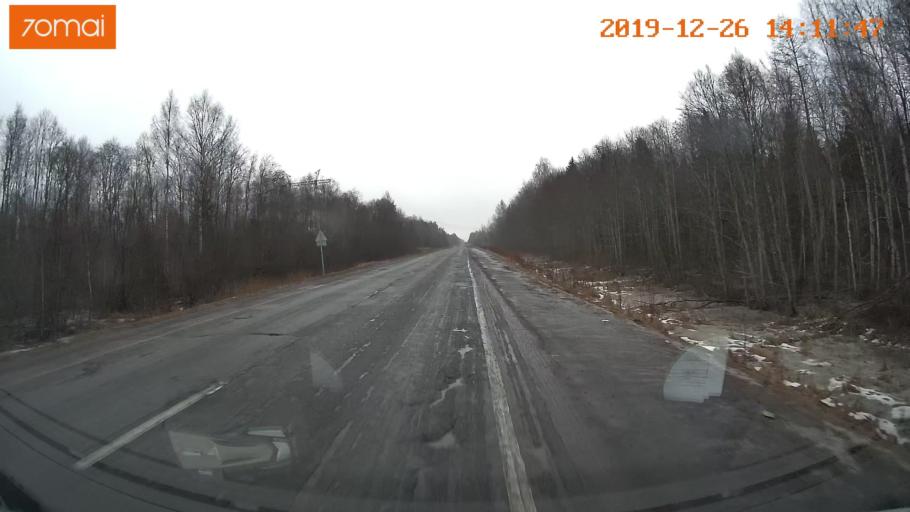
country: RU
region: Jaroslavl
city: Poshekhon'ye
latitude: 58.5101
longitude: 38.9785
